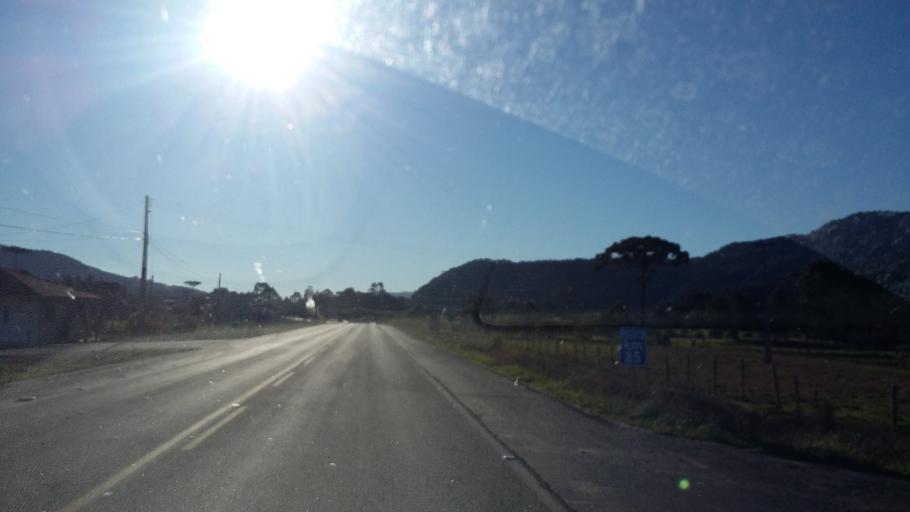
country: BR
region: Santa Catarina
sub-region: Lauro Muller
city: Lauro Muller
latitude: -28.0210
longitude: -49.5021
